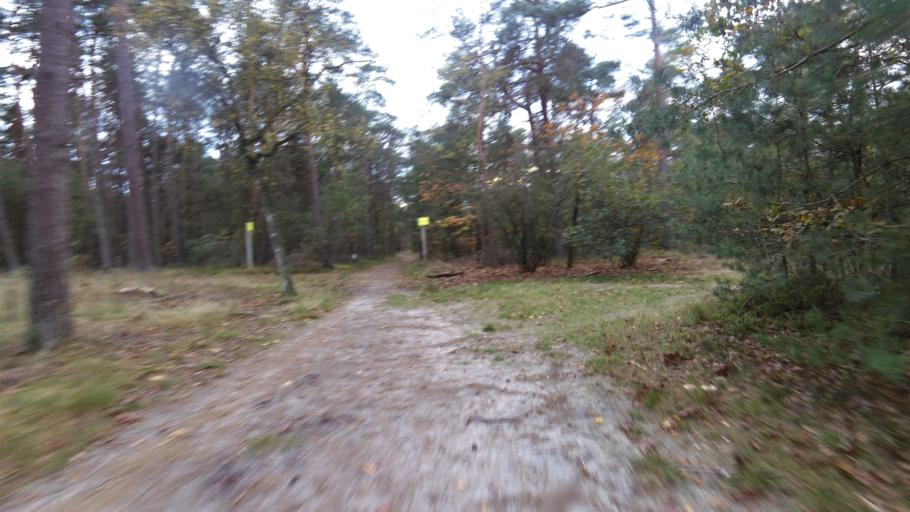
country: NL
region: Gelderland
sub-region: Gemeente Elburg
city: Elburg
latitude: 52.4053
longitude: 5.8701
